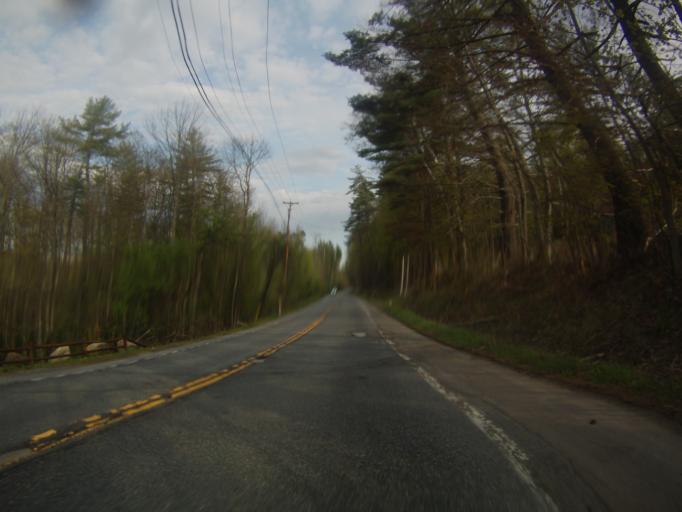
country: US
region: New York
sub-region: Warren County
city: Warrensburg
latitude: 43.6615
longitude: -73.9553
